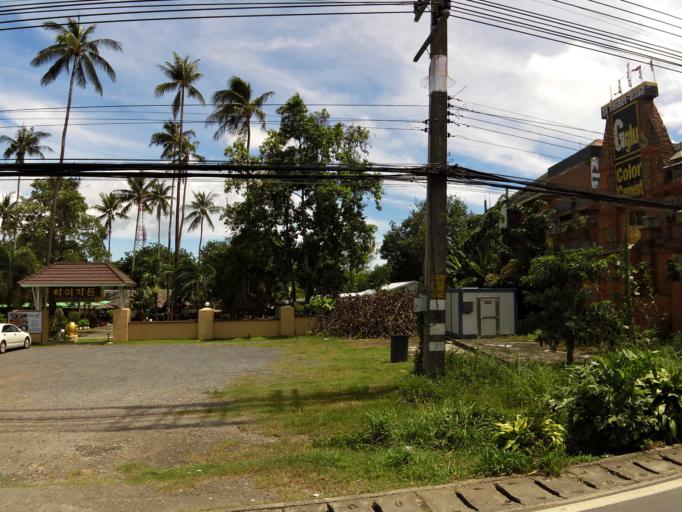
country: TH
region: Phuket
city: Mueang Phuket
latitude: 7.8646
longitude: 98.3477
